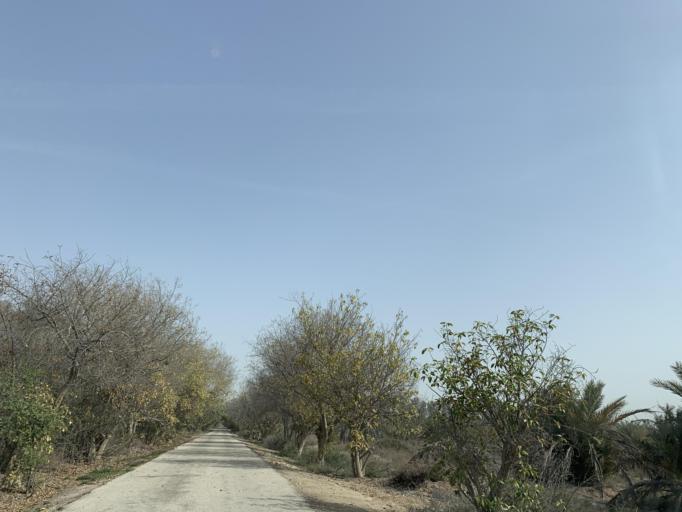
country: BH
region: Northern
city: Madinat `Isa
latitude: 26.1630
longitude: 50.5310
